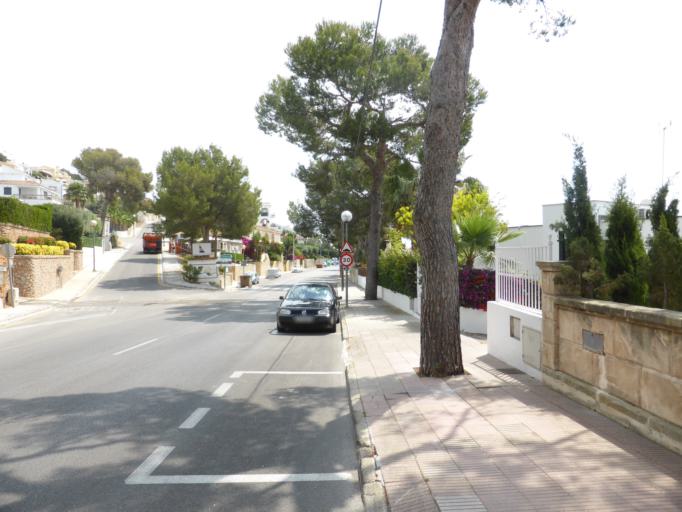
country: ES
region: Balearic Islands
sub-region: Illes Balears
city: Port d'Alcudia
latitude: 39.8368
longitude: 3.1455
